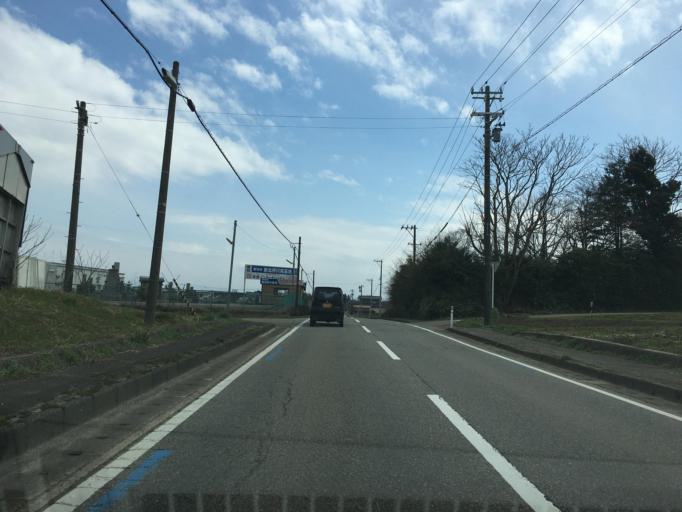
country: JP
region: Toyama
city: Kuragaki-kosugi
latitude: 36.6788
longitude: 137.1237
